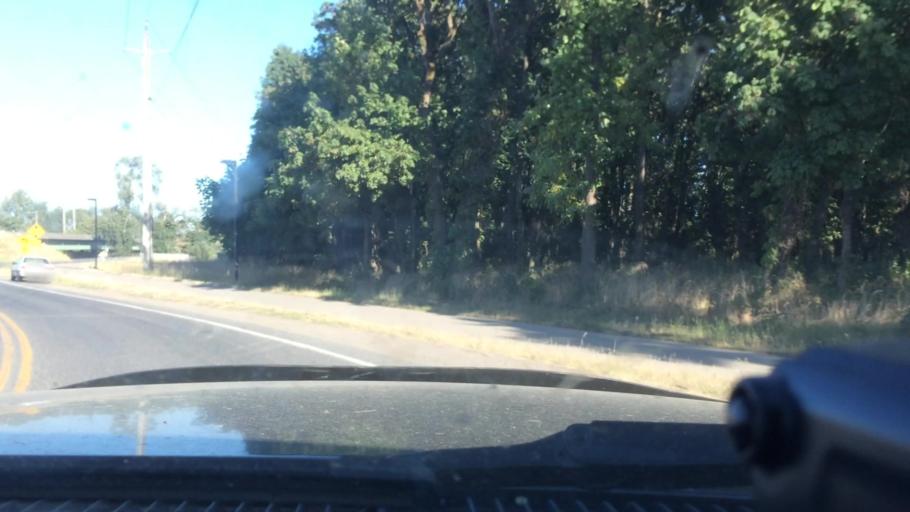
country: US
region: Oregon
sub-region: Lane County
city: Eugene
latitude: 44.0962
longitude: -123.1101
